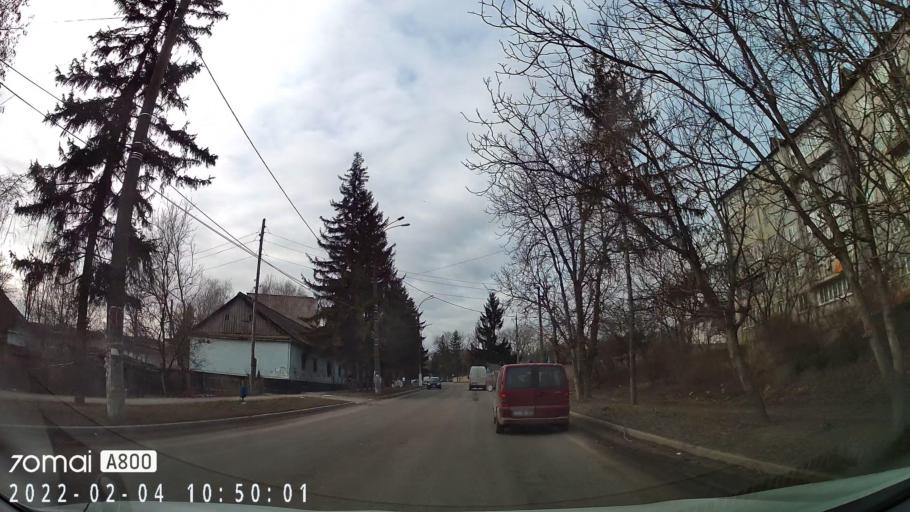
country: MD
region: Briceni
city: Briceni
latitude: 48.3561
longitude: 27.0882
